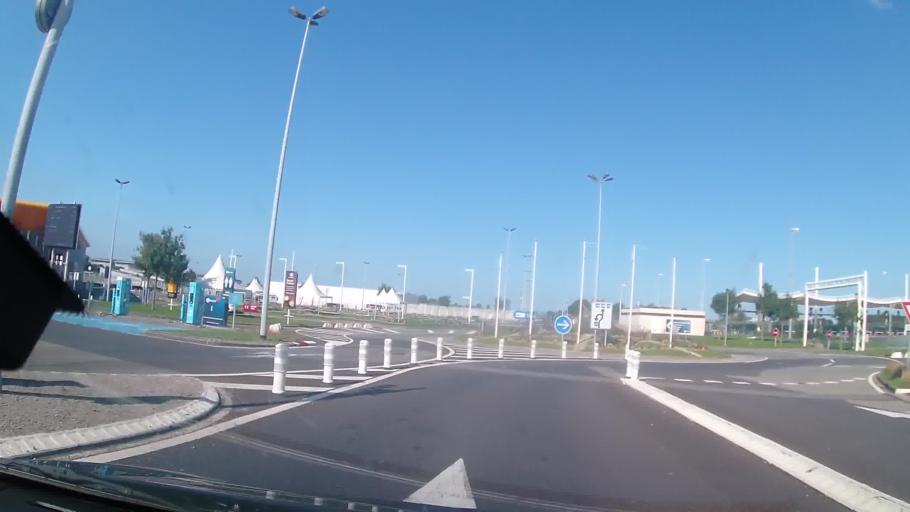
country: FR
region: Nord-Pas-de-Calais
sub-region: Departement du Pas-de-Calais
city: Coquelles
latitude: 50.9338
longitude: 1.8128
